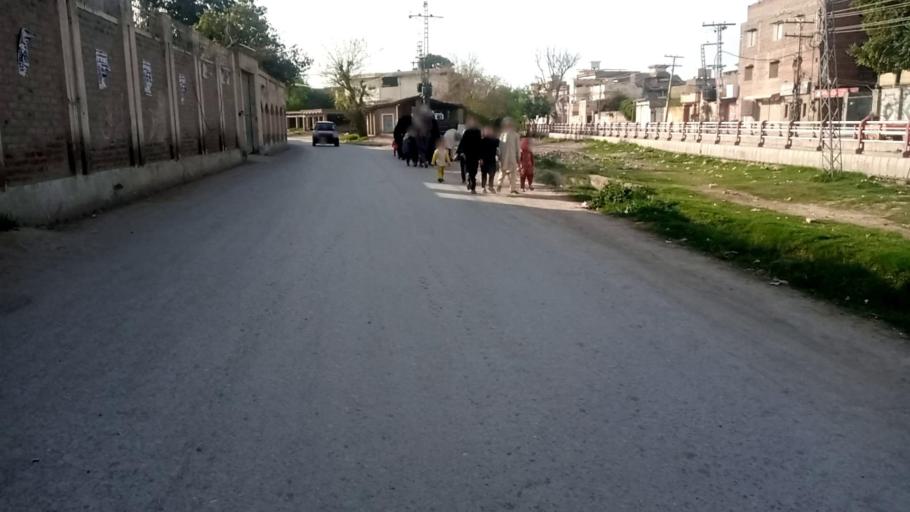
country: PK
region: Khyber Pakhtunkhwa
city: Peshawar
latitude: 34.0112
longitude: 71.6152
